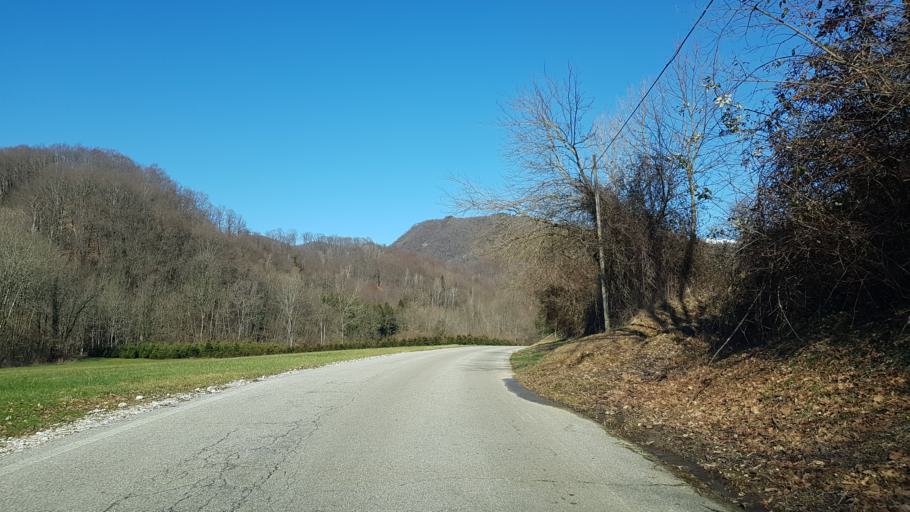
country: IT
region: Friuli Venezia Giulia
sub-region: Provincia di Udine
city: Nimis
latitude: 46.2091
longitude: 13.2923
